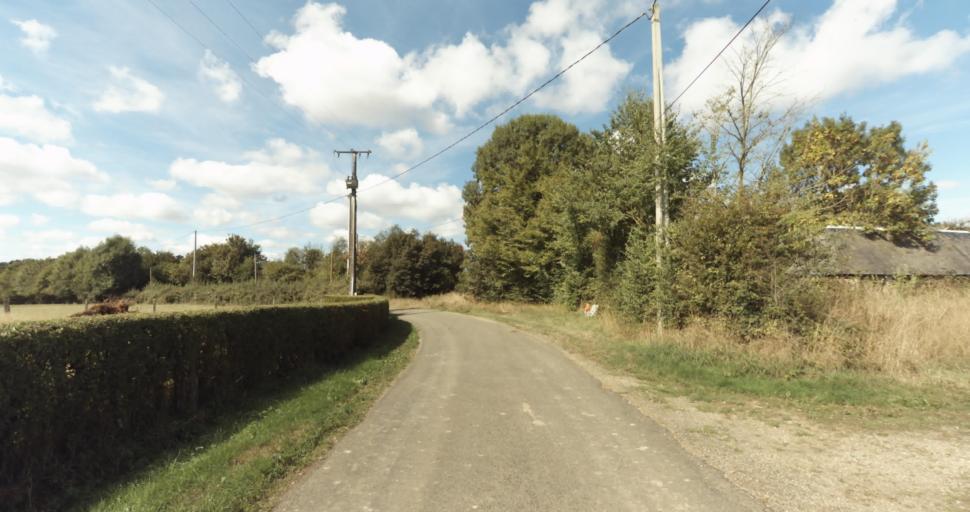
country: FR
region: Lower Normandy
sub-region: Departement du Calvados
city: Orbec
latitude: 48.9257
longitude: 0.3740
